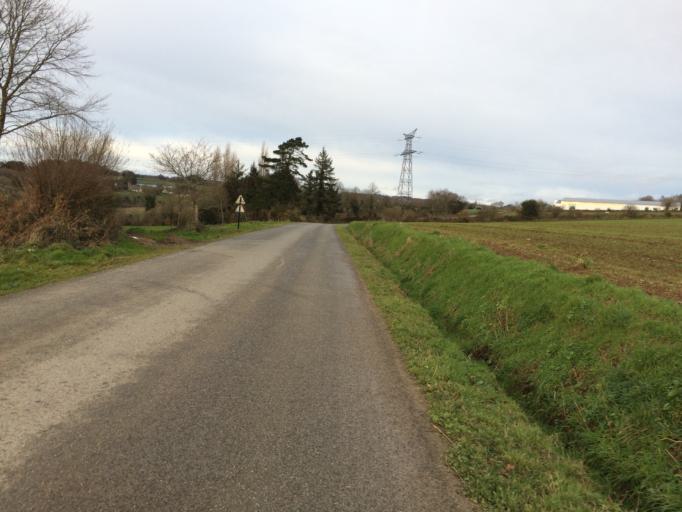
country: FR
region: Brittany
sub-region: Departement du Finistere
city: Saint-Urbain
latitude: 48.3859
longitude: -4.2362
